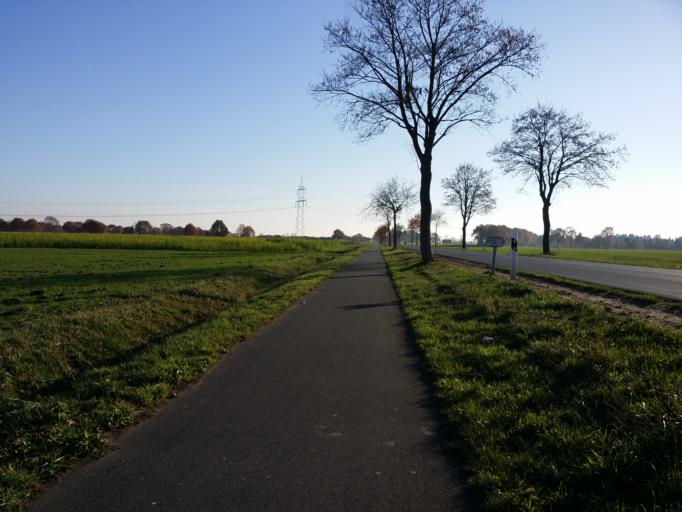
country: DE
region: Lower Saxony
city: Langwedel
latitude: 53.0250
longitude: 9.1641
